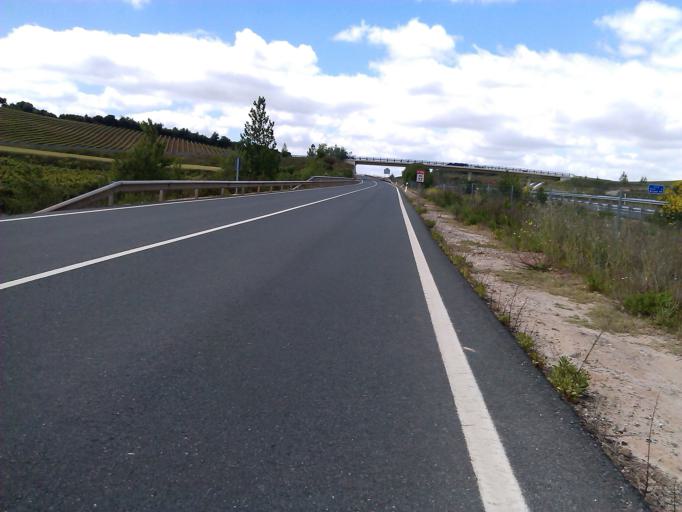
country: ES
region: La Rioja
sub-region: Provincia de La Rioja
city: Ventosa
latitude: 42.4158
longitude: -2.6351
